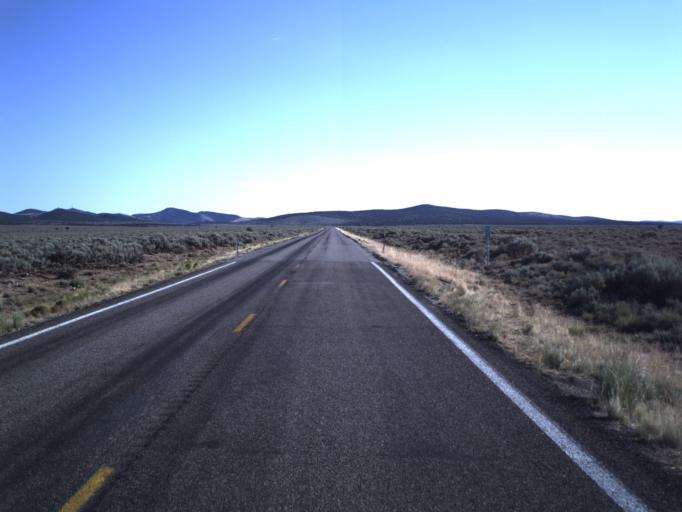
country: US
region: Utah
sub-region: Iron County
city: Enoch
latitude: 37.9863
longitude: -113.0020
